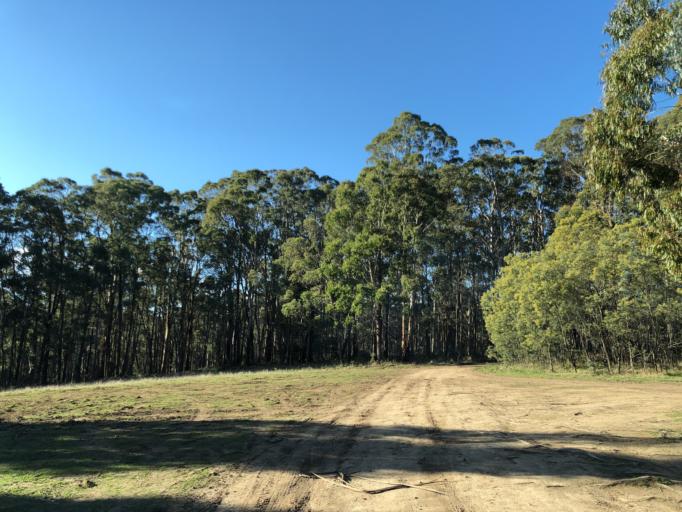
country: AU
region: Victoria
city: Brown Hill
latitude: -37.4979
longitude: 144.1694
